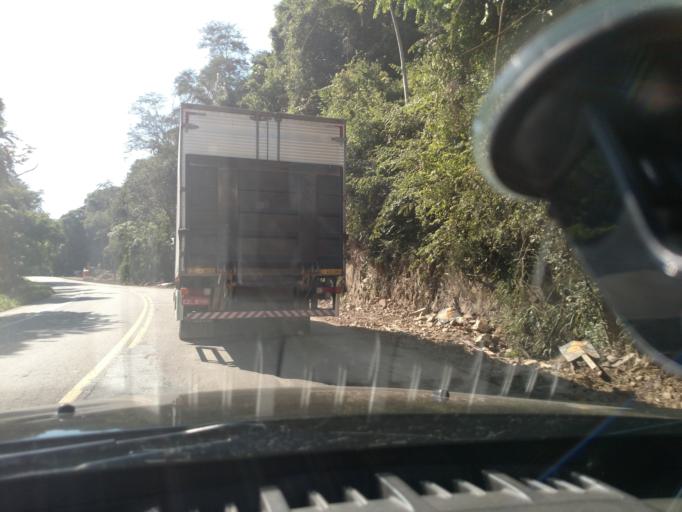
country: BR
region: Santa Catarina
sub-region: Ibirama
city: Ibirama
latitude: -27.0942
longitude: -49.4668
